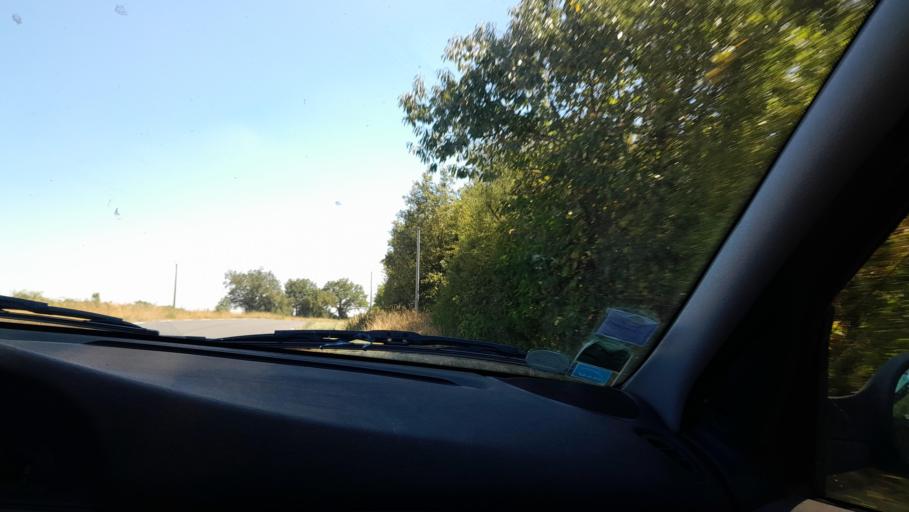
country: FR
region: Pays de la Loire
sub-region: Departement de la Loire-Atlantique
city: Saint-Mars-la-Jaille
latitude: 47.5968
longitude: -1.1974
